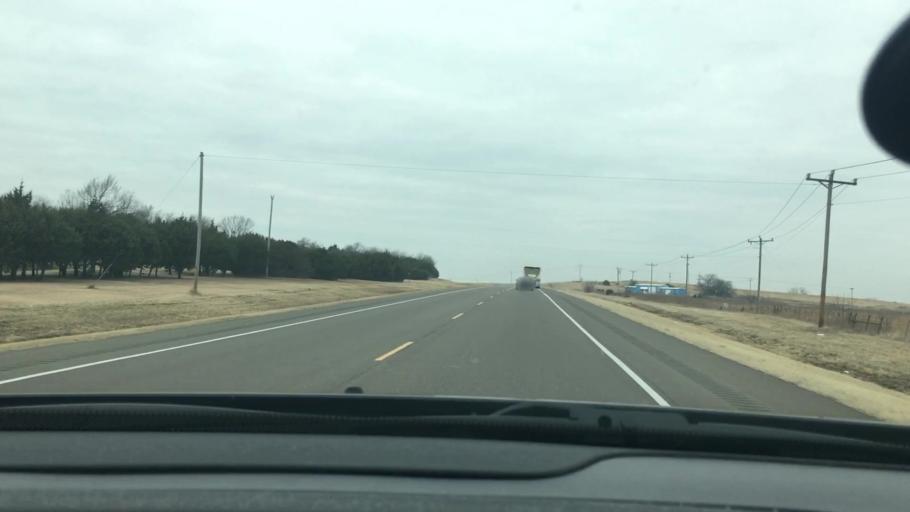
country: US
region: Oklahoma
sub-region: Murray County
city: Davis
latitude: 34.5179
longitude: -97.2078
